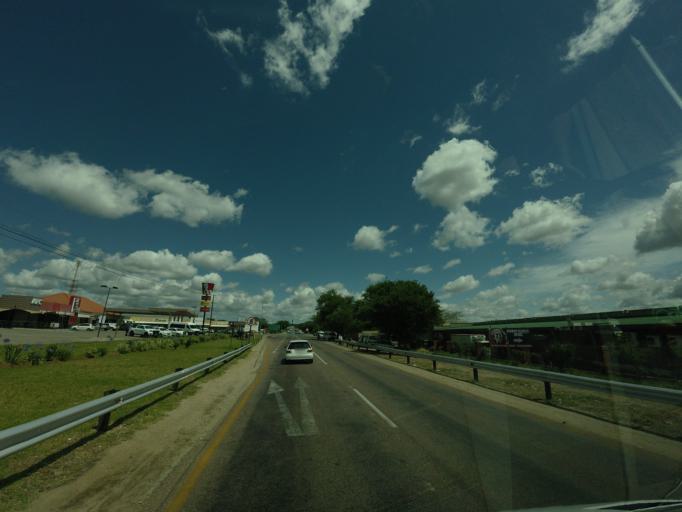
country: ZA
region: Limpopo
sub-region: Mopani District Municipality
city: Hoedspruit
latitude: -24.3519
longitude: 30.9571
